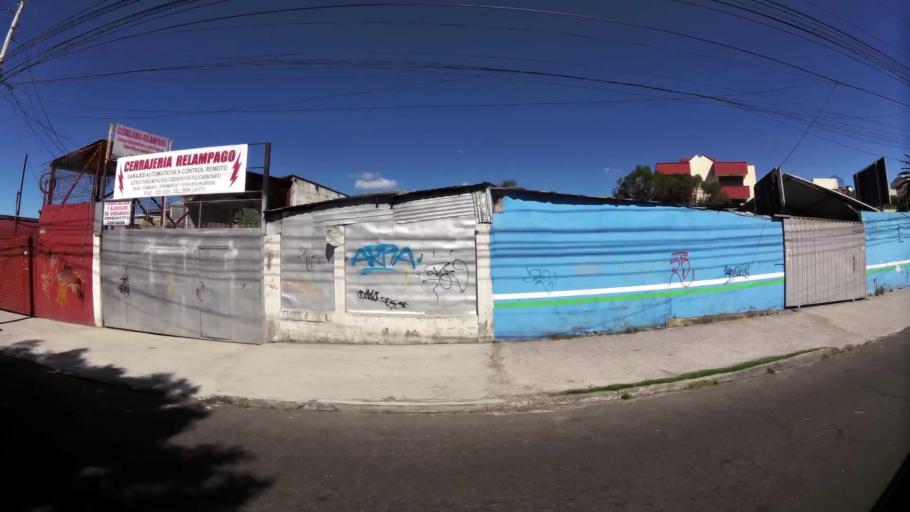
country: EC
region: Pichincha
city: Quito
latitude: -0.1425
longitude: -78.4700
